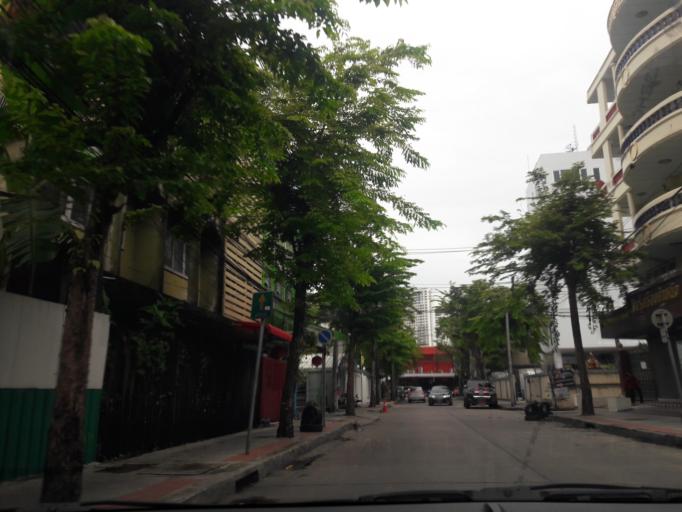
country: TH
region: Bangkok
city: Khlong San
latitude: 13.7272
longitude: 100.4993
